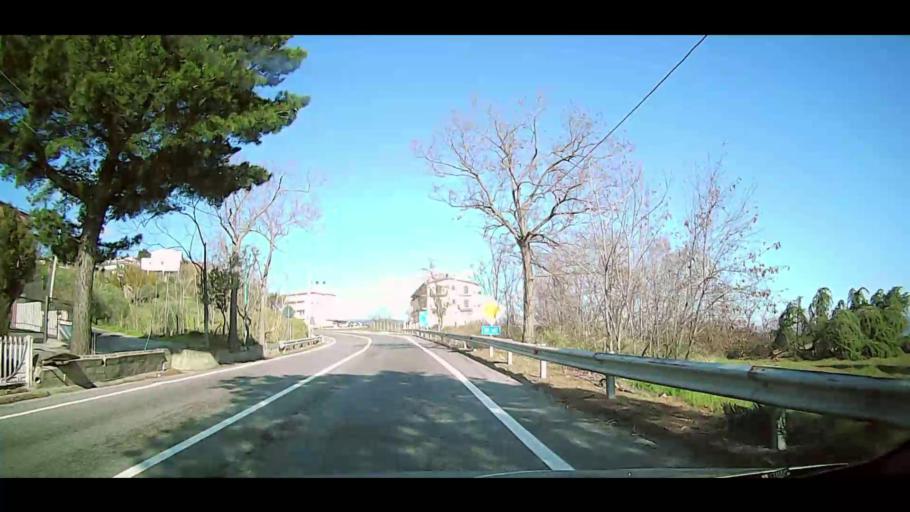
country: IT
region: Calabria
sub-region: Provincia di Crotone
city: Cerenzia
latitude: 39.2466
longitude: 16.7900
